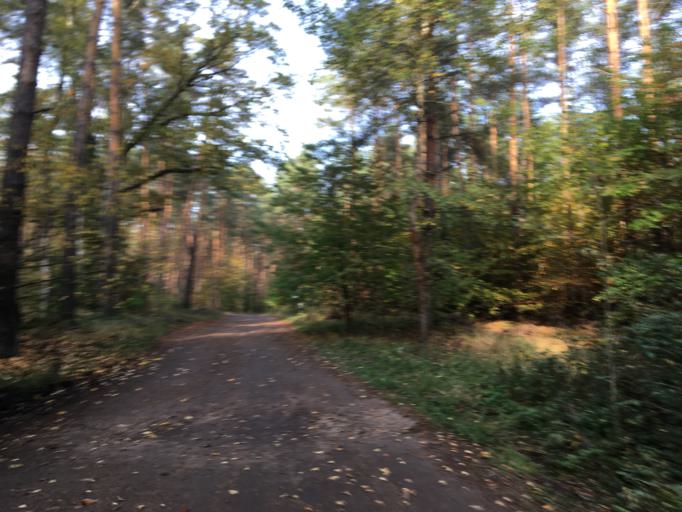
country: DE
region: Brandenburg
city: Glienicke
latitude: 52.6797
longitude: 13.3385
